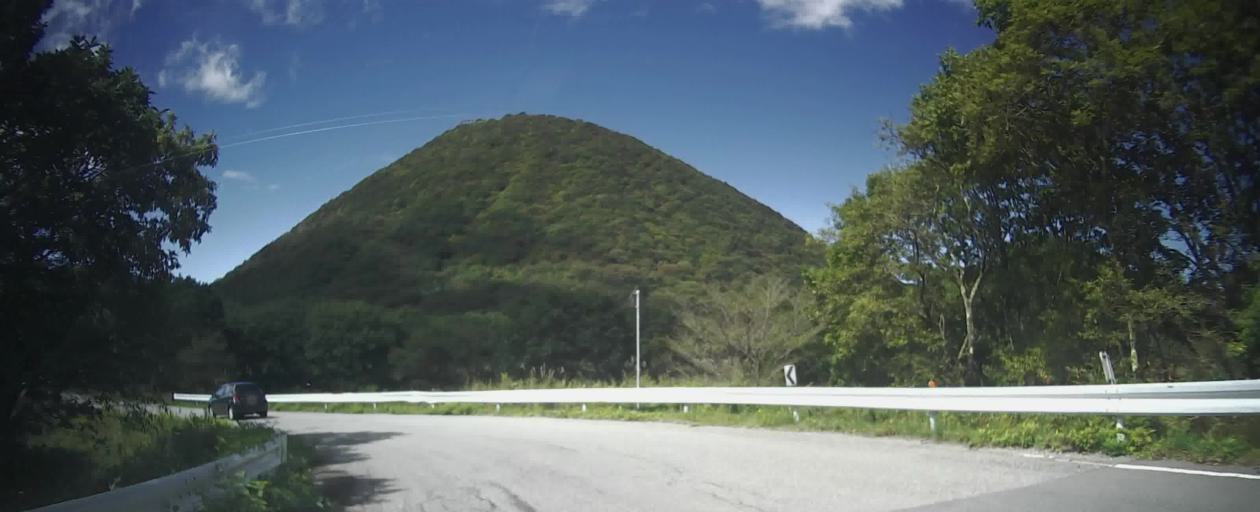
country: JP
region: Gunma
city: Shibukawa
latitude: 36.4698
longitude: 138.8840
